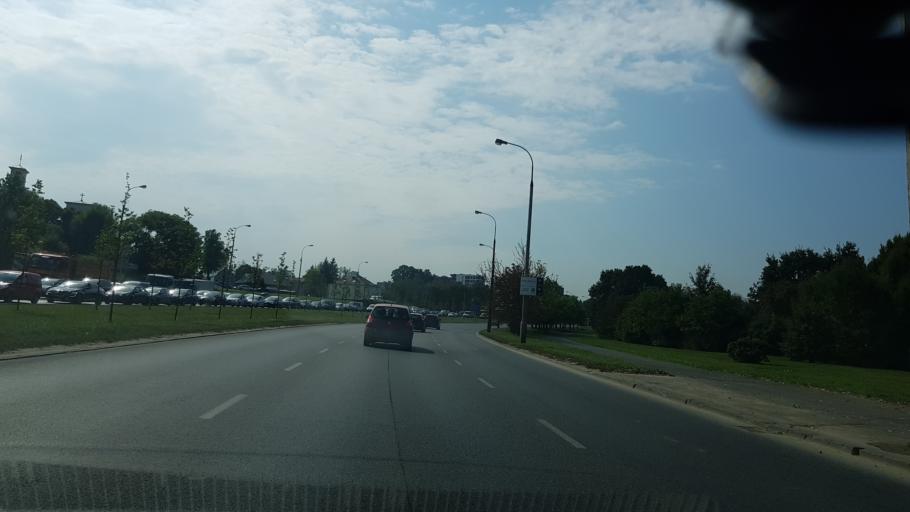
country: PL
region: Masovian Voivodeship
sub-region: Warszawa
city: Mokotow
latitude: 52.1739
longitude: 21.0438
